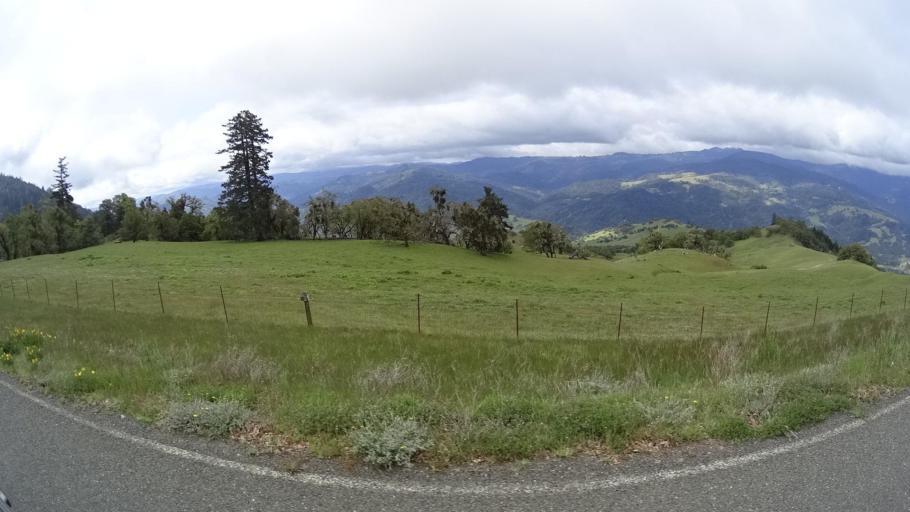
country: US
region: California
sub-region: Humboldt County
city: Redway
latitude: 40.1547
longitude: -123.5581
